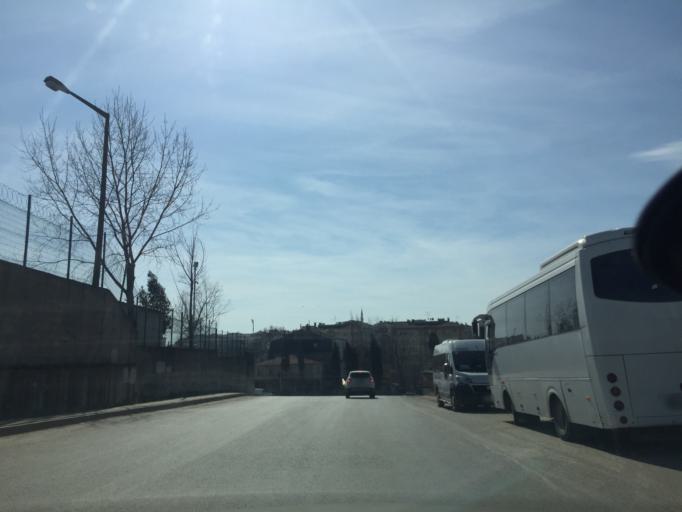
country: TR
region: Istanbul
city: Icmeler
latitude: 40.8371
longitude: 29.3152
